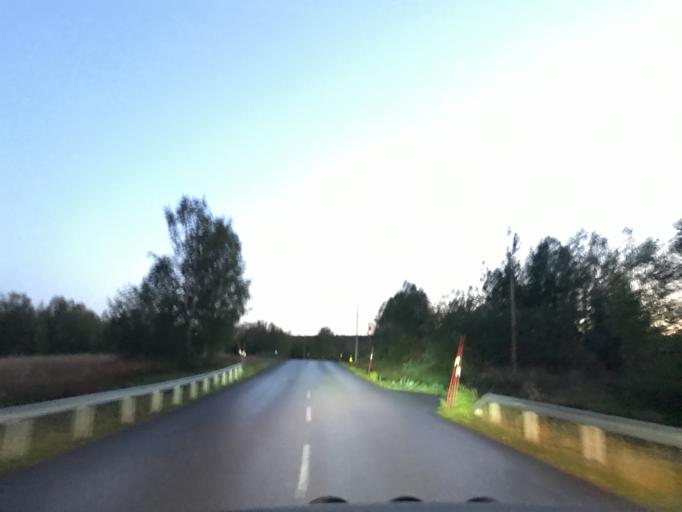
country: SE
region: Norrbotten
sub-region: Gallivare Kommun
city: Malmberget
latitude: 67.6515
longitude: 21.0355
